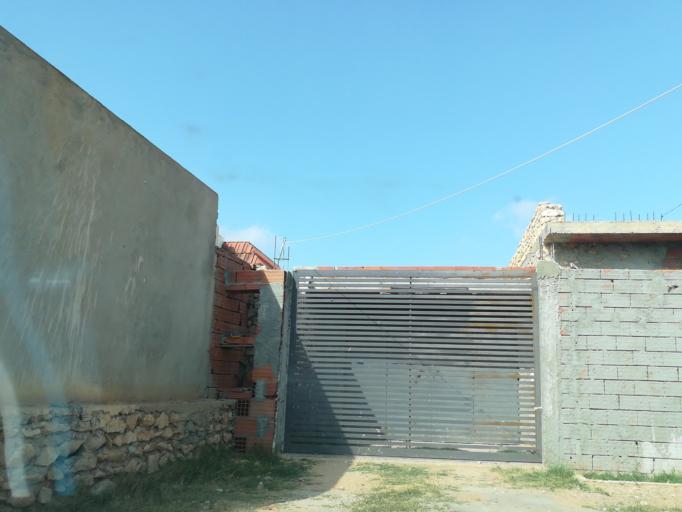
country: TN
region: Safaqis
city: Al Qarmadah
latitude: 34.8169
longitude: 10.7546
